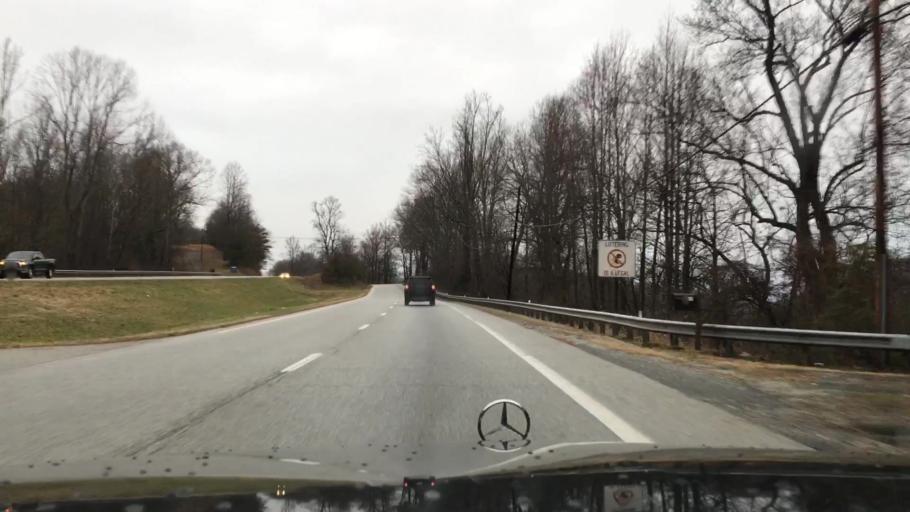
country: US
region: Virginia
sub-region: Nelson County
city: Nellysford
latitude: 37.8386
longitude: -78.8299
